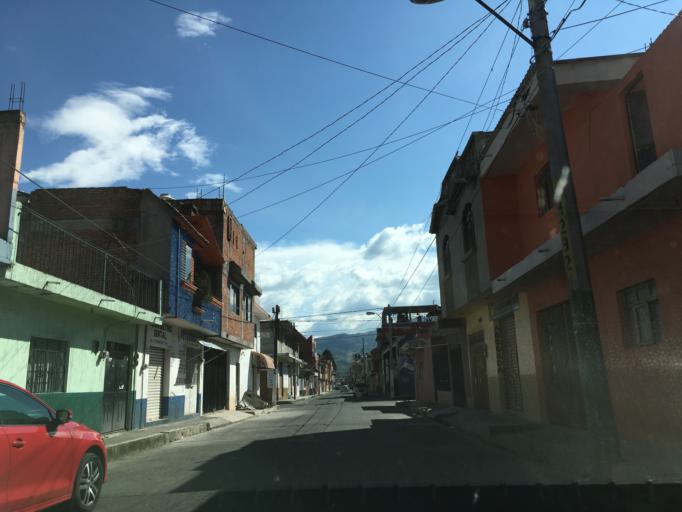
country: MX
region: Michoacan
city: Zacapu
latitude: 19.8175
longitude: -101.7849
